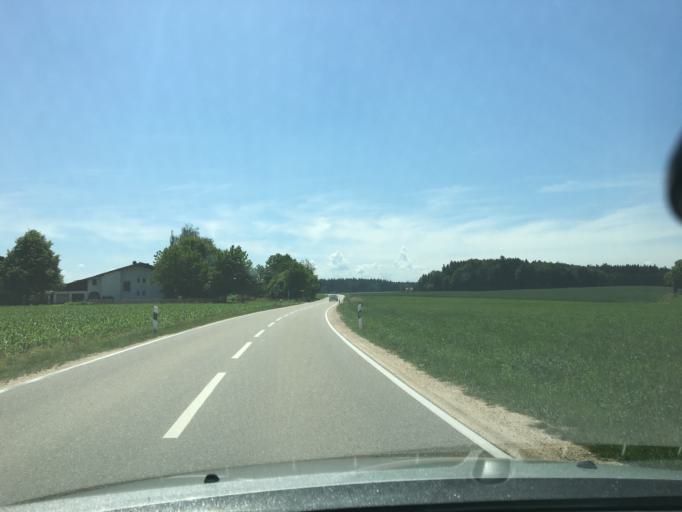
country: DE
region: Bavaria
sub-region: Upper Bavaria
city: Halsbach
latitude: 48.1103
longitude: 12.6839
